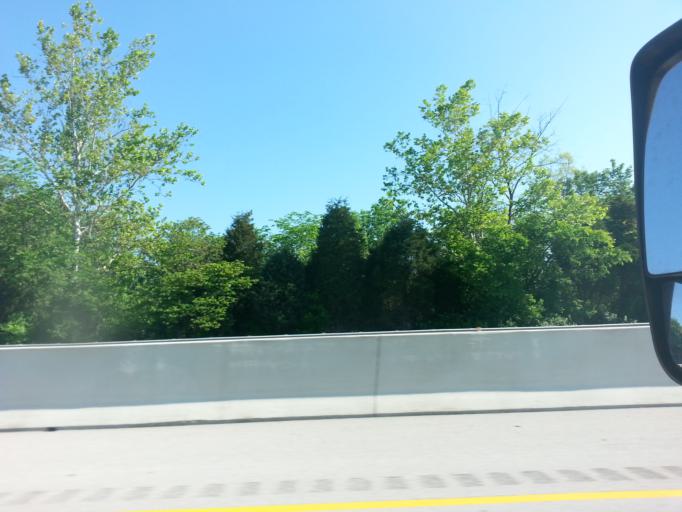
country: US
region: Kentucky
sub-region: Jefferson County
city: Middletown
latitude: 38.2205
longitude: -85.4502
